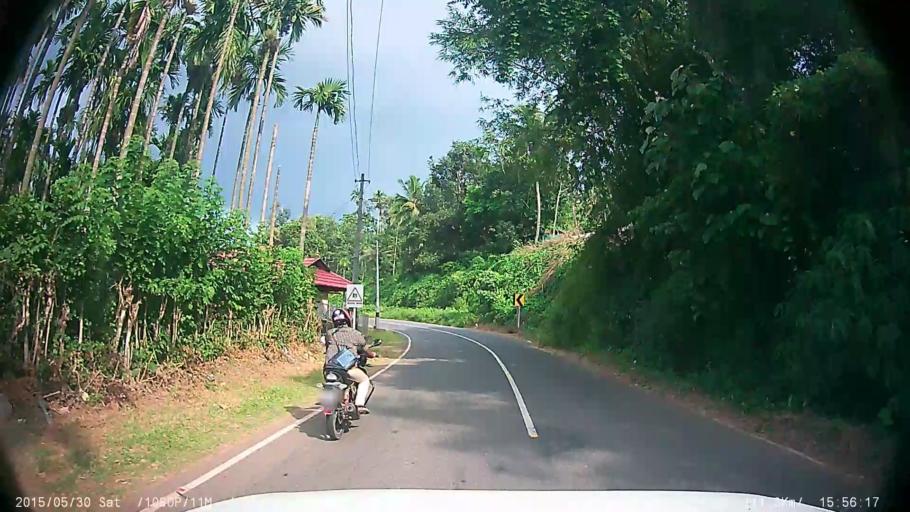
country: IN
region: Kerala
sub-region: Wayanad
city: Kalpetta
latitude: 11.6603
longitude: 76.0841
